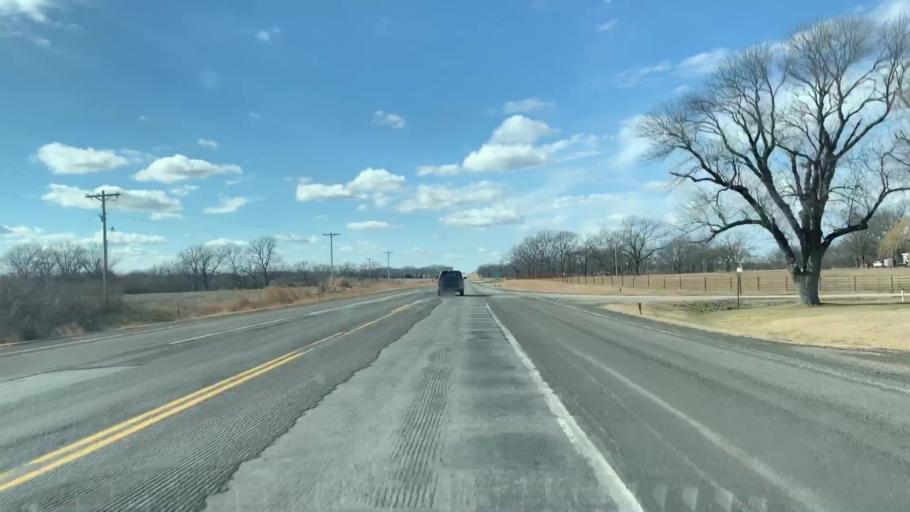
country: US
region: Kansas
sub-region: Labette County
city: Parsons
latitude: 37.3404
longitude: -95.1306
